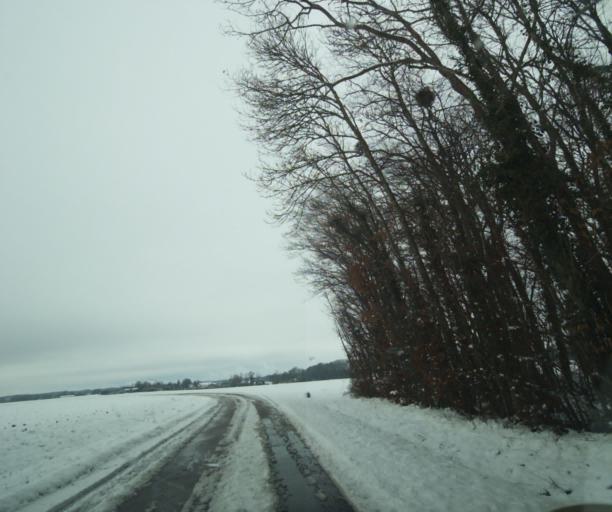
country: FR
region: Champagne-Ardenne
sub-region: Departement de la Haute-Marne
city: Montier-en-Der
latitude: 48.4632
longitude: 4.6509
